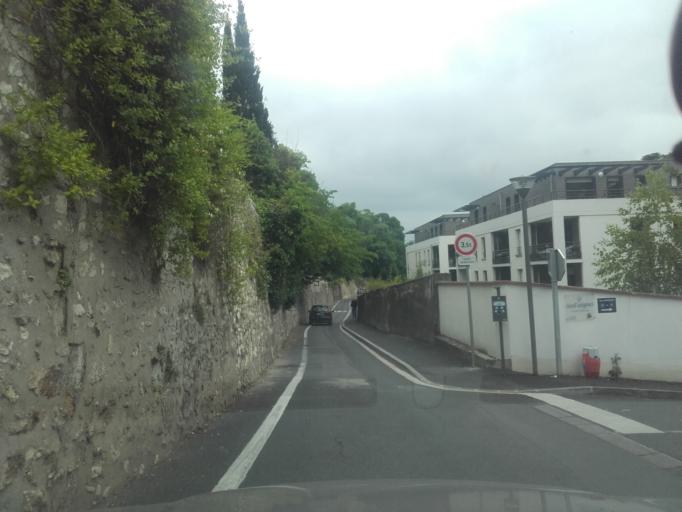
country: FR
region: Centre
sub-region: Departement d'Indre-et-Loire
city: Saint-Cyr-sur-Loire
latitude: 47.4047
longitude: 0.6866
